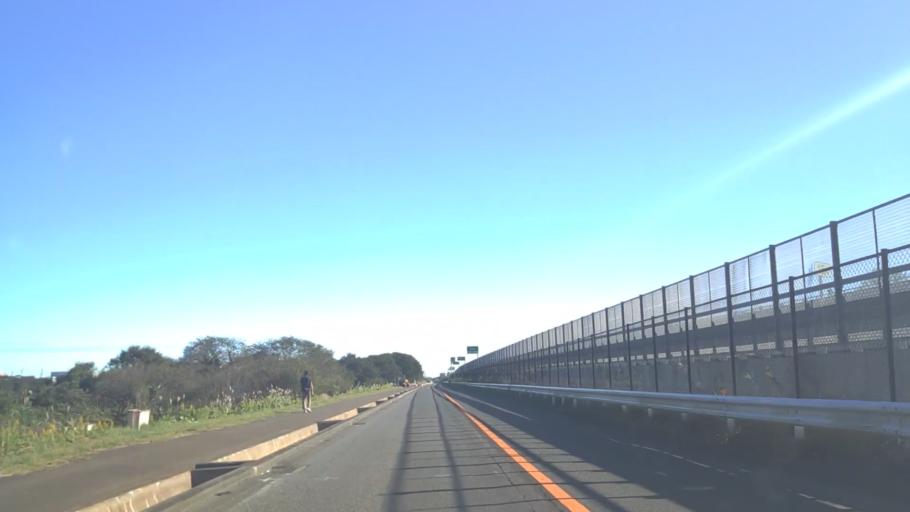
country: JP
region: Kanagawa
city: Zama
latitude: 35.4744
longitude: 139.3753
